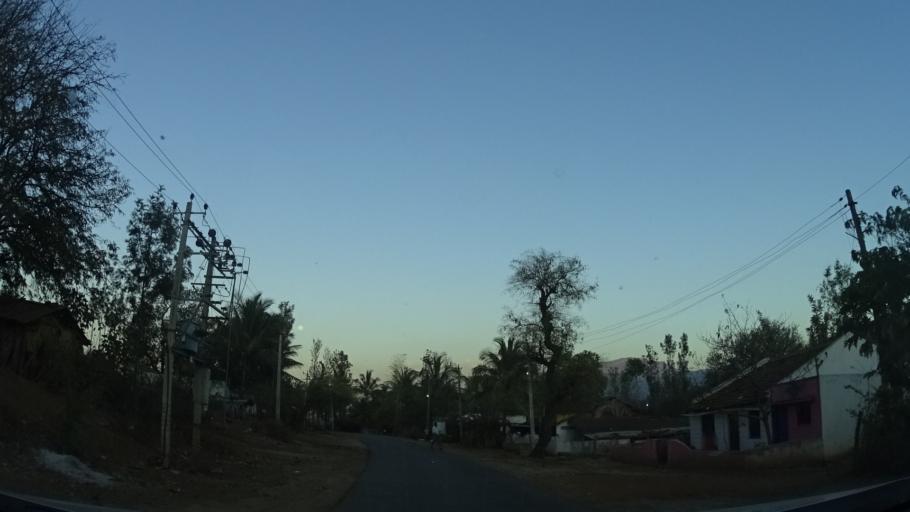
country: IN
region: Karnataka
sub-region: Chikmagalur
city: Tarikere
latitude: 13.5660
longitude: 75.8029
